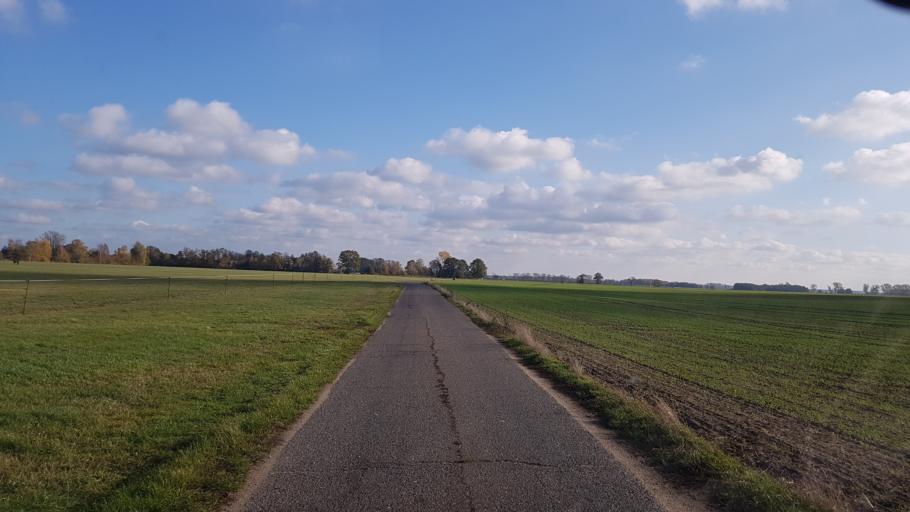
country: DE
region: Brandenburg
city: Doberlug-Kirchhain
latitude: 51.6909
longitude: 13.5212
